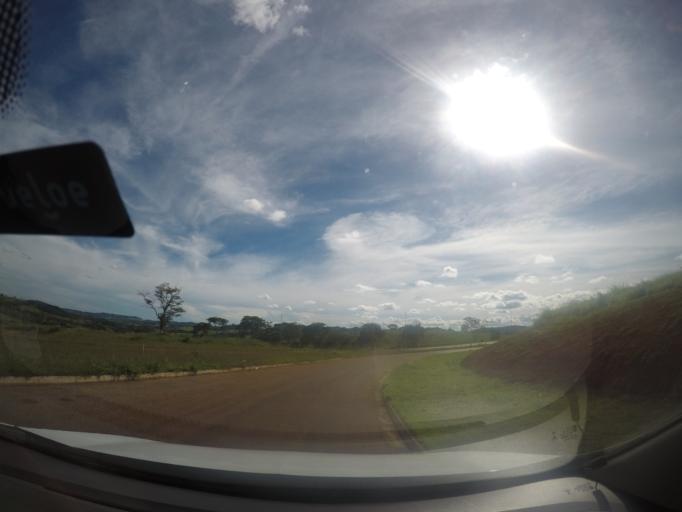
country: BR
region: Goias
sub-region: Inhumas
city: Inhumas
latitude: -16.4117
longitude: -49.4736
